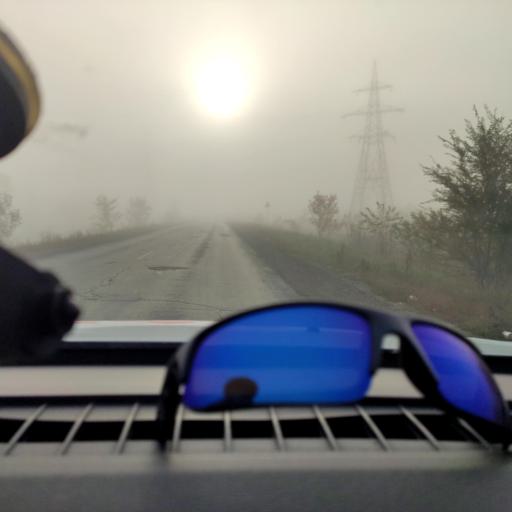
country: RU
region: Samara
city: Chapayevsk
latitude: 53.0033
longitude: 49.7512
